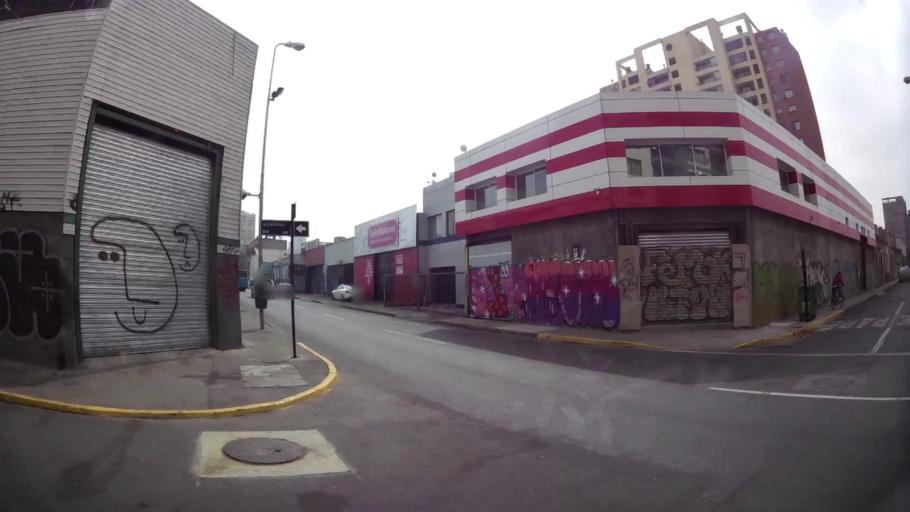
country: CL
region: Santiago Metropolitan
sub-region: Provincia de Santiago
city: Santiago
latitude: -33.4587
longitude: -70.6536
